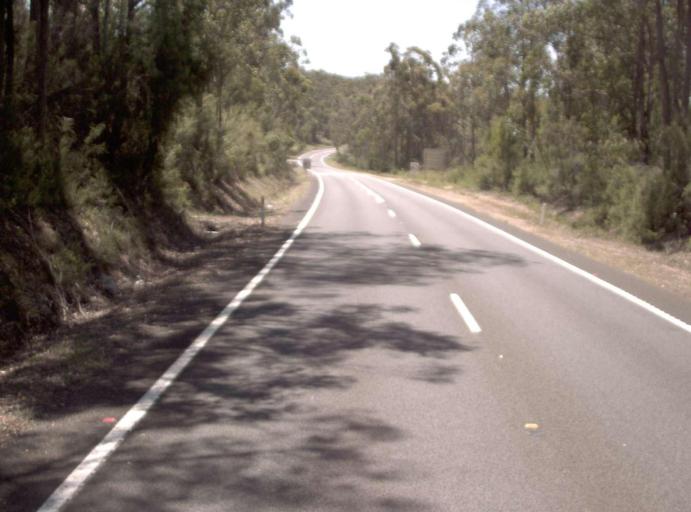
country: AU
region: Victoria
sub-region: East Gippsland
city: Lakes Entrance
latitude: -37.7379
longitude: 148.0808
